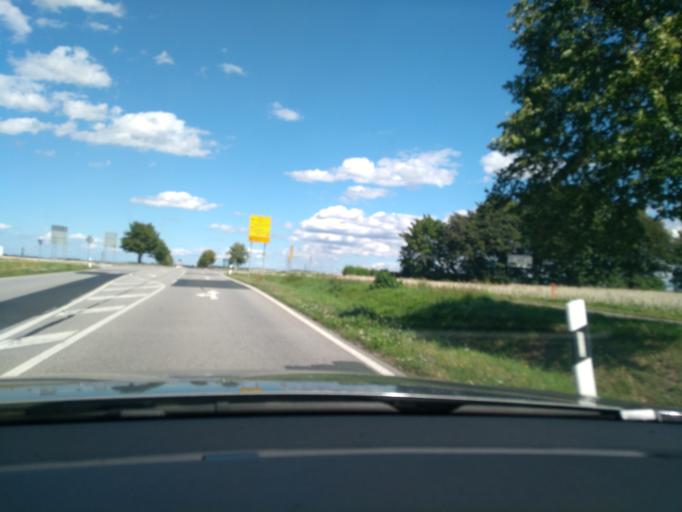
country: DE
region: Saxony
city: Goda
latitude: 51.1707
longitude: 14.2917
